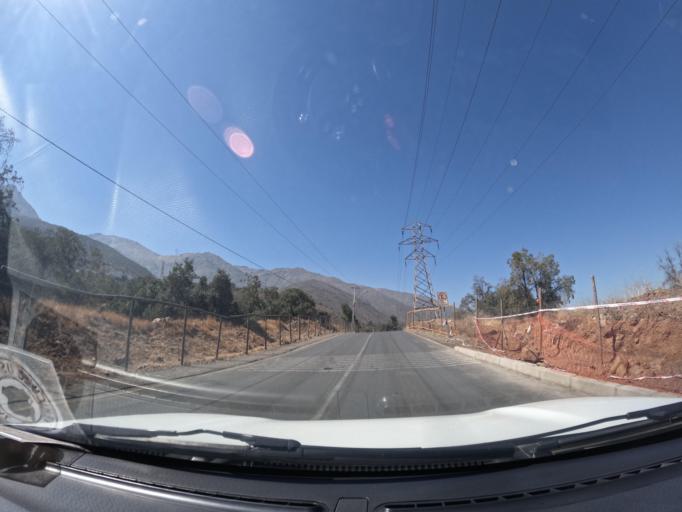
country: CL
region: Santiago Metropolitan
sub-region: Provincia de Santiago
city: Villa Presidente Frei, Nunoa, Santiago, Chile
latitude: -33.4905
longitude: -70.5190
